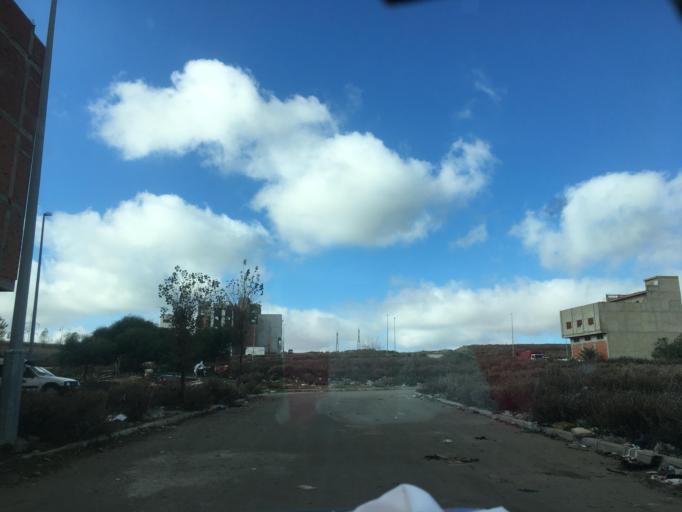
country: MA
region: Tanger-Tetouan
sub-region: Tanger-Assilah
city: Tangier
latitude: 35.7093
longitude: -5.8162
